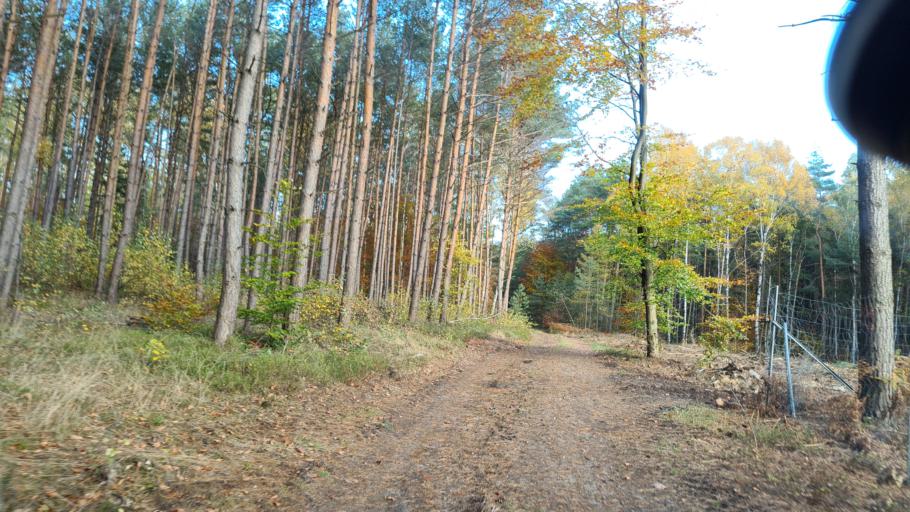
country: DE
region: Saxony
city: Dahlen
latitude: 51.4215
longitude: 13.0079
